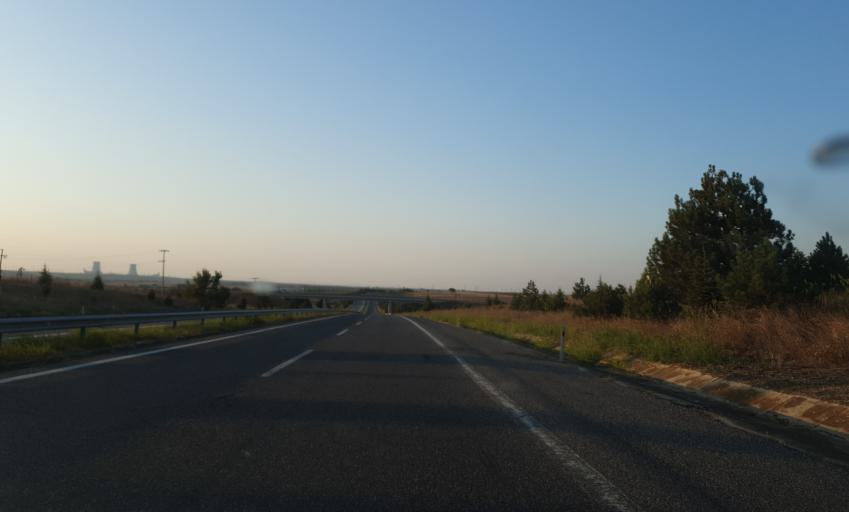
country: TR
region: Kirklareli
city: Luleburgaz
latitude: 41.4166
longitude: 27.3876
